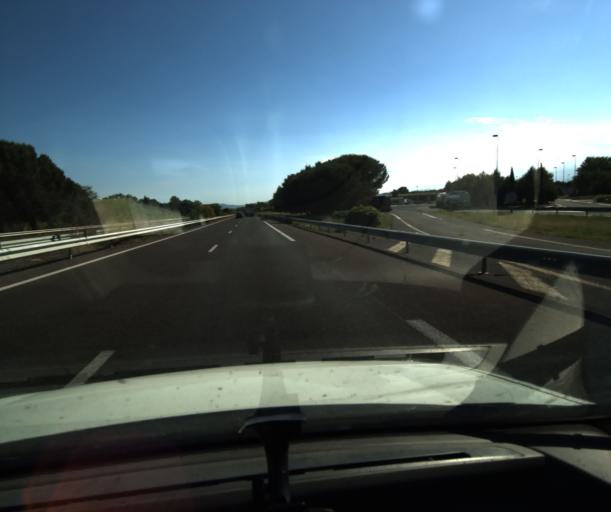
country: FR
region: Languedoc-Roussillon
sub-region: Departement des Pyrenees-Orientales
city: Villemolaque
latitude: 42.5841
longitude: 2.8466
